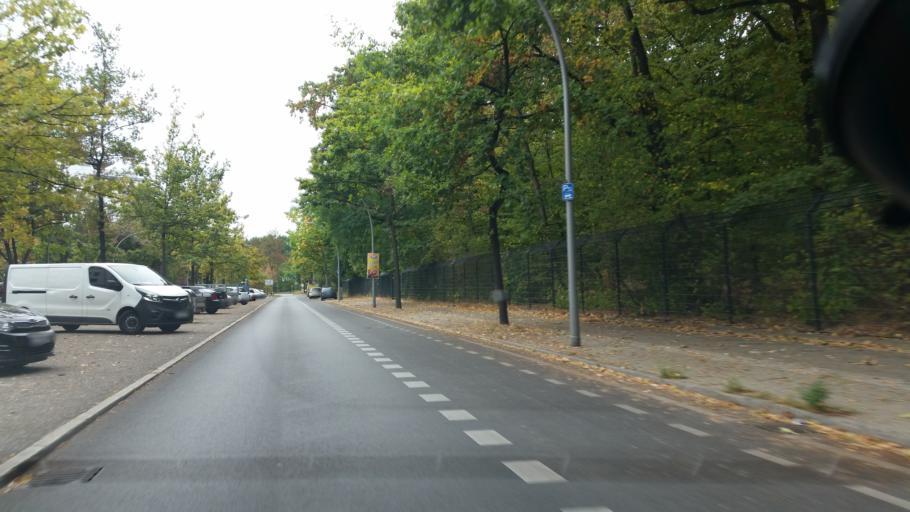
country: DE
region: Berlin
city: Mariendorf
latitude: 52.4422
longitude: 13.3971
